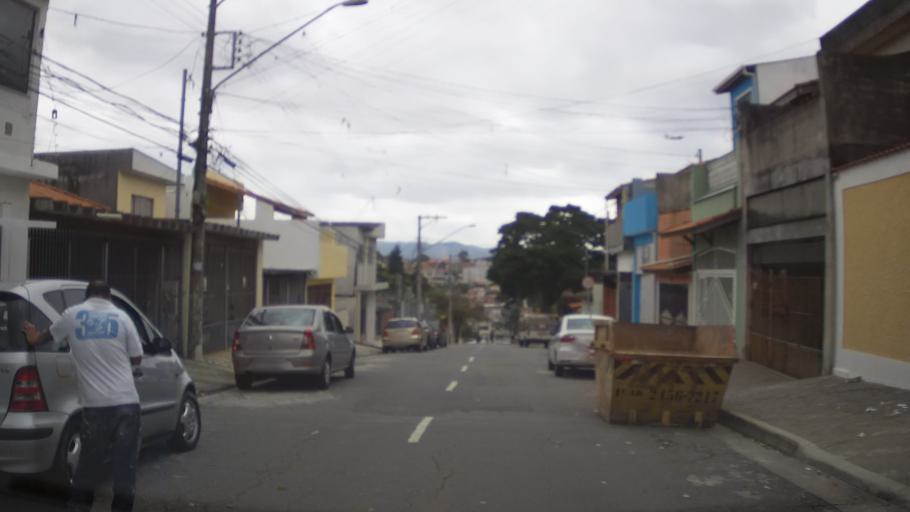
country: BR
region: Sao Paulo
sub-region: Guarulhos
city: Guarulhos
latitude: -23.4508
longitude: -46.5112
